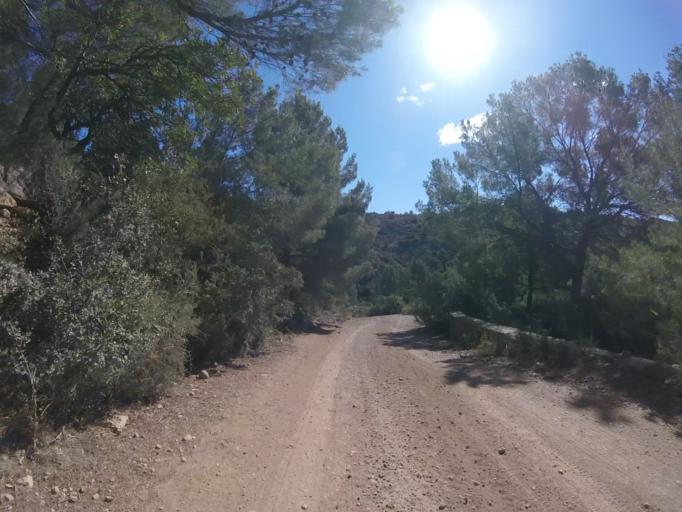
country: ES
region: Valencia
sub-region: Provincia de Castello
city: Benicassim
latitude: 40.0734
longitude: 0.0782
